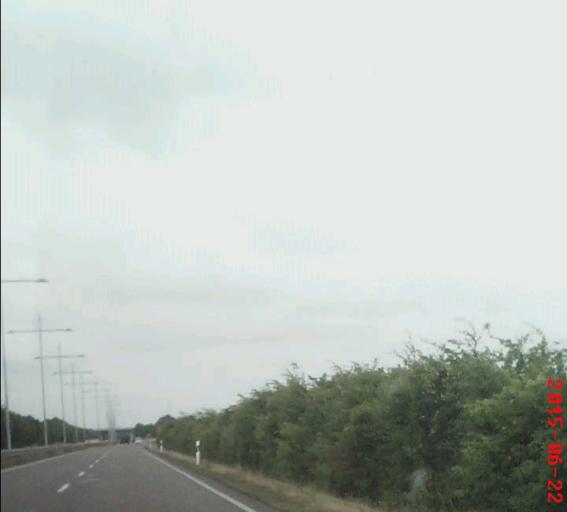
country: DE
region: Saxony
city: Schkeuditz
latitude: 51.4213
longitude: 12.2350
